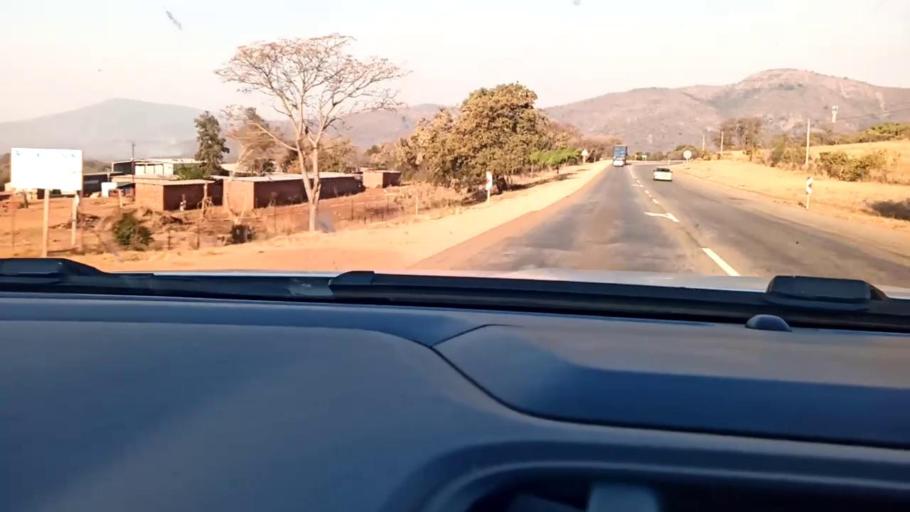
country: ZA
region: Limpopo
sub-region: Mopani District Municipality
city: Duiwelskloof
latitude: -23.6453
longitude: 30.1655
